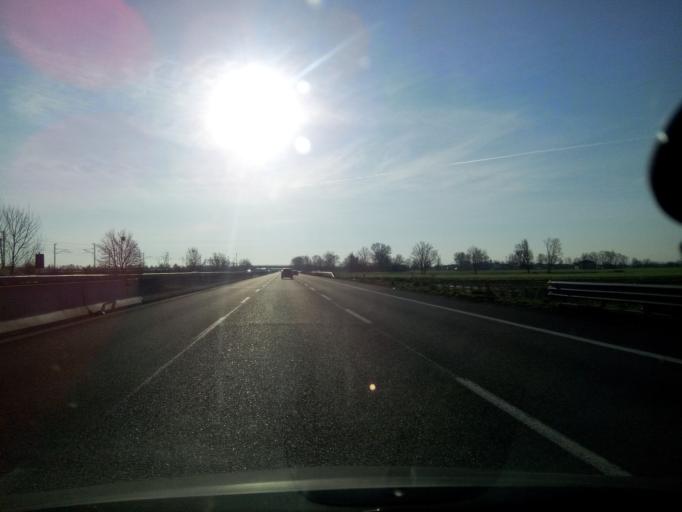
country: IT
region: Emilia-Romagna
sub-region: Provincia di Parma
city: Fontanellato
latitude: 44.8800
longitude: 10.1496
